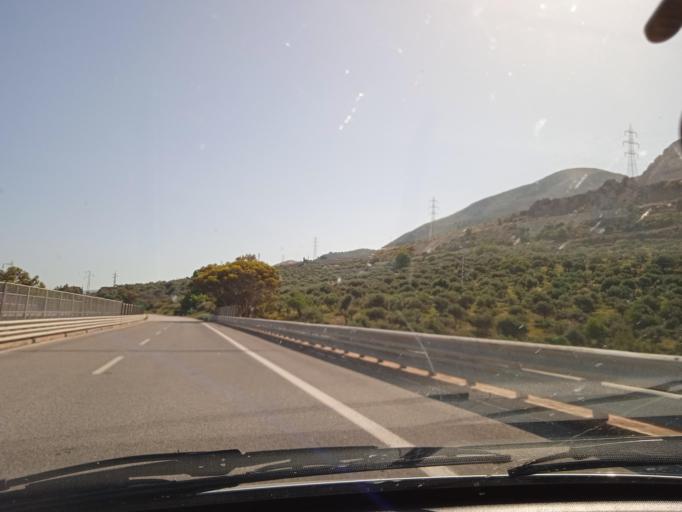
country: IT
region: Sicily
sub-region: Messina
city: Torrenova
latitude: 38.0856
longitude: 14.6899
